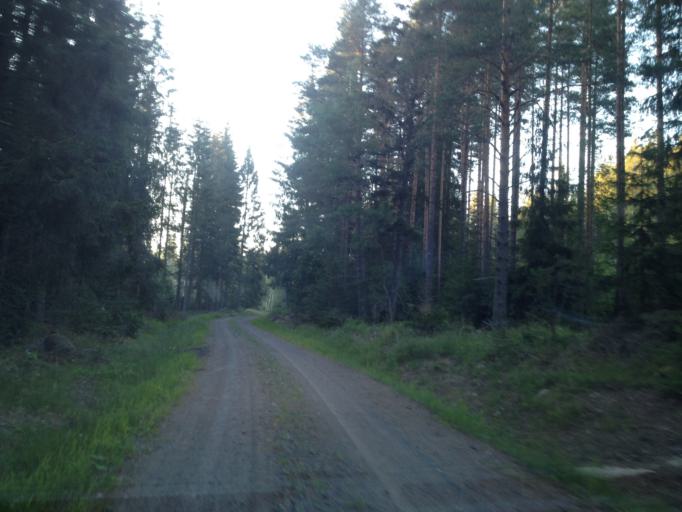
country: SE
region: Kalmar
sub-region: Vasterviks Kommun
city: Overum
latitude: 58.0050
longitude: 16.1221
